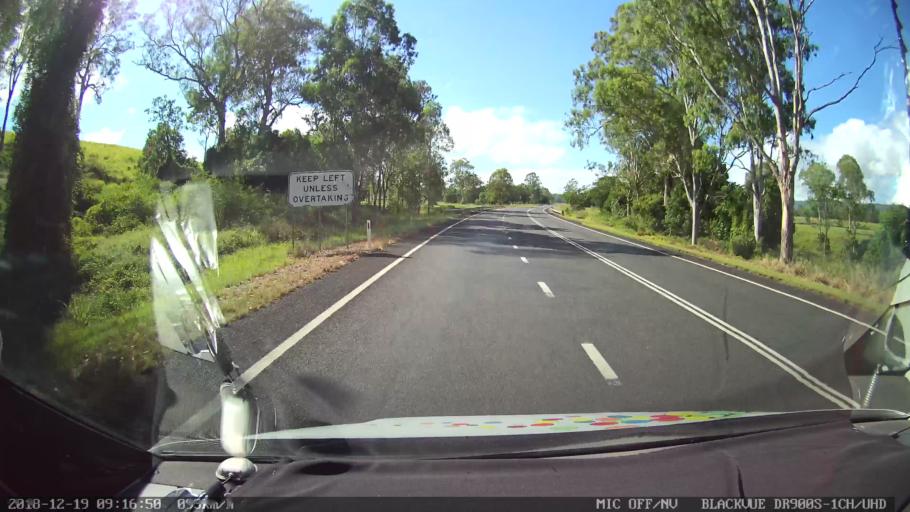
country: AU
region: New South Wales
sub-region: Kyogle
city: Kyogle
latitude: -28.5254
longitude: 152.9707
